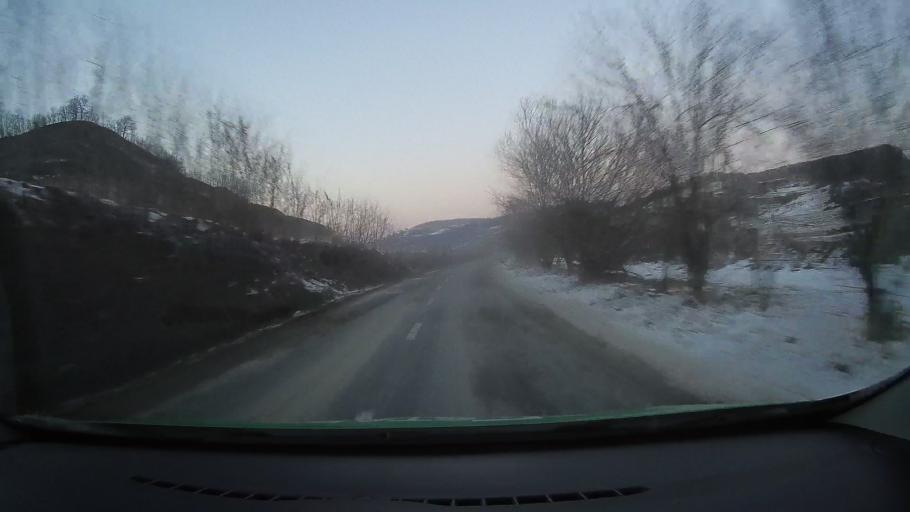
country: RO
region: Sibiu
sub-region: Comuna Atel
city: Atel
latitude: 46.1709
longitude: 24.4689
